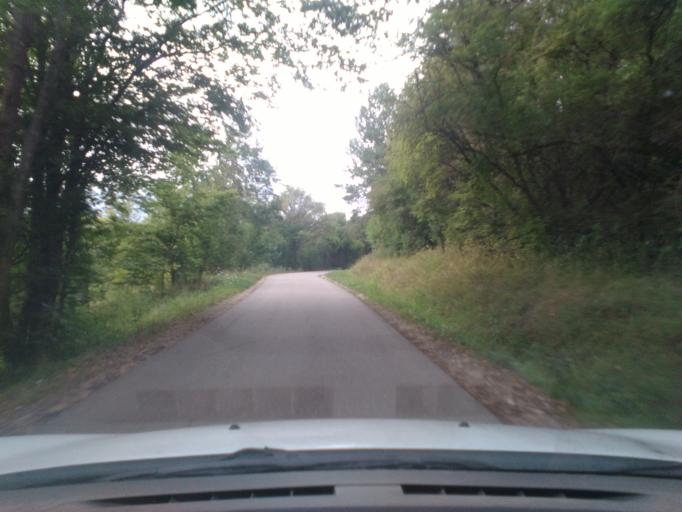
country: FR
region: Lorraine
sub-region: Departement des Vosges
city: Portieux
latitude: 48.3336
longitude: 6.3595
